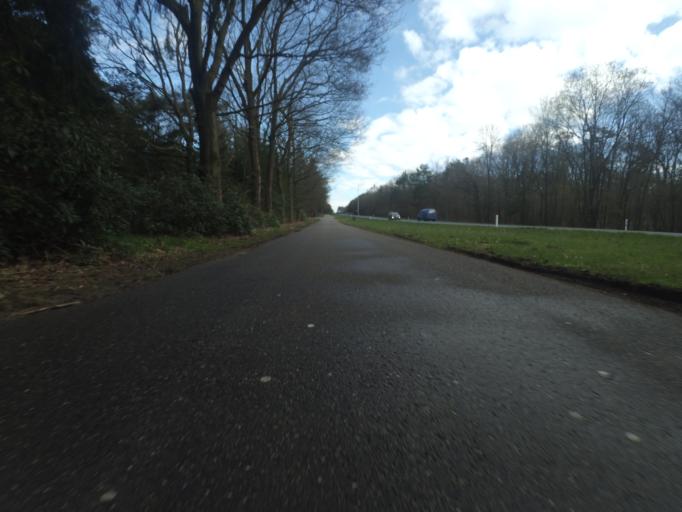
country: NL
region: Gelderland
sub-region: Gemeente Apeldoorn
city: Beekbergen
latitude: 52.1354
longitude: 5.9586
